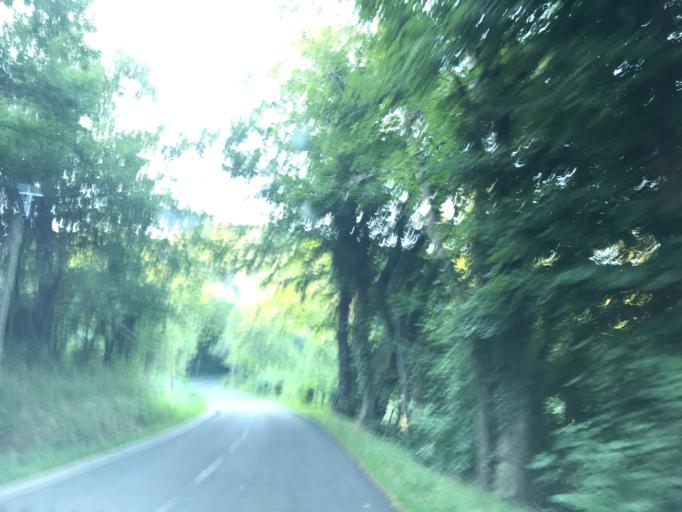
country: FR
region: Auvergne
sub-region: Departement du Puy-de-Dome
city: Thiers
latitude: 45.8674
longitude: 3.5577
